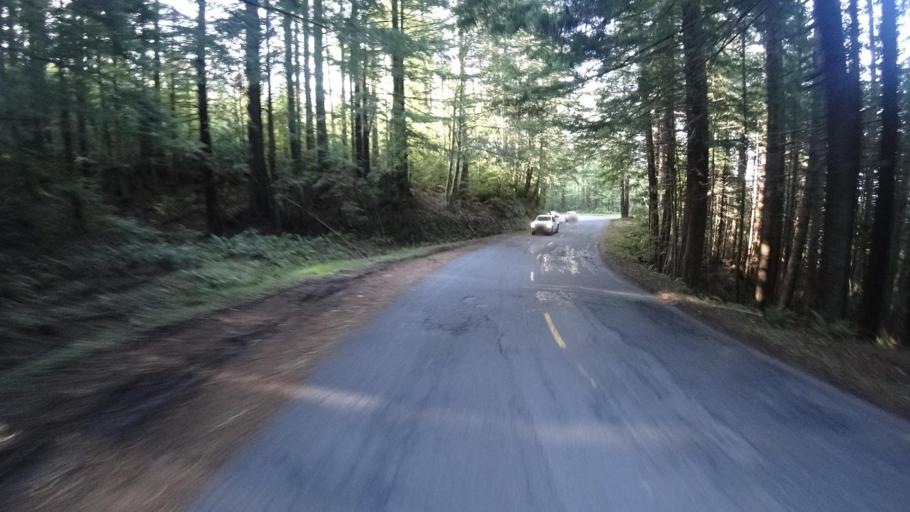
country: US
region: California
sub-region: Humboldt County
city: Bayside
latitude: 40.7612
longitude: -124.0004
